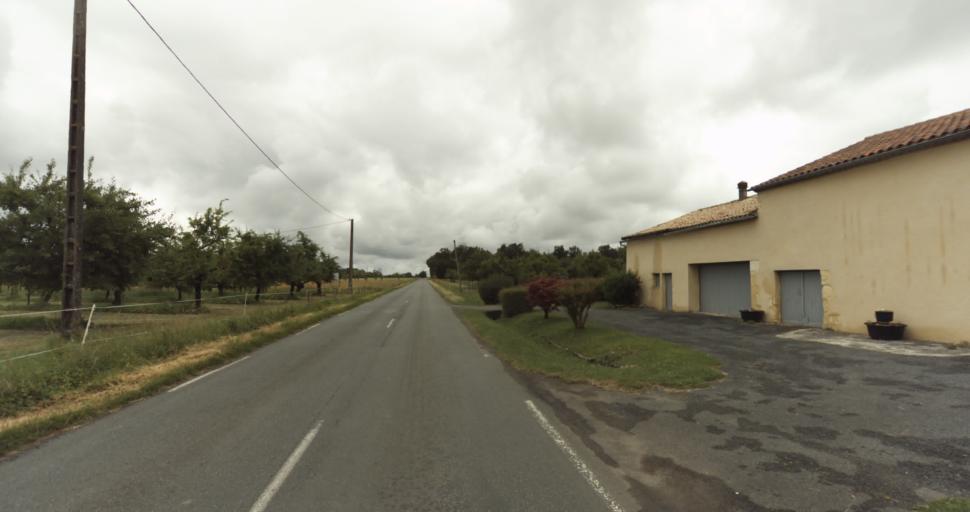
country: FR
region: Aquitaine
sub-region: Departement de la Dordogne
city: Beaumont-du-Perigord
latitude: 44.7415
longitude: 0.7816
